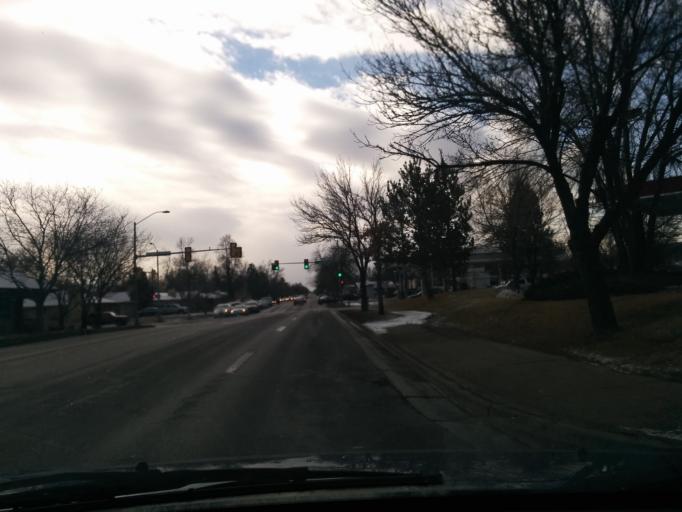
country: US
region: Colorado
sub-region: Larimer County
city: Fort Collins
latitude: 40.5752
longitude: -105.1151
